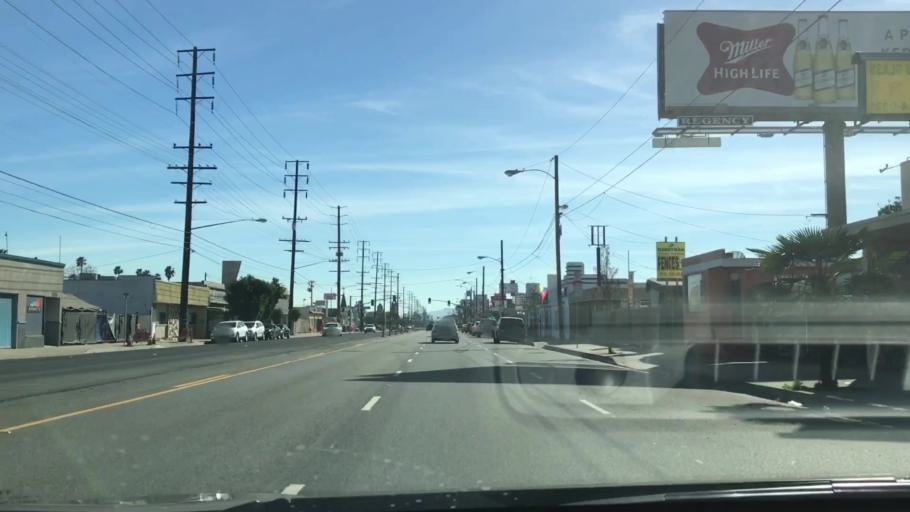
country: US
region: California
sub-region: Los Angeles County
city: Alondra Park
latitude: 33.8928
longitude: -118.3266
